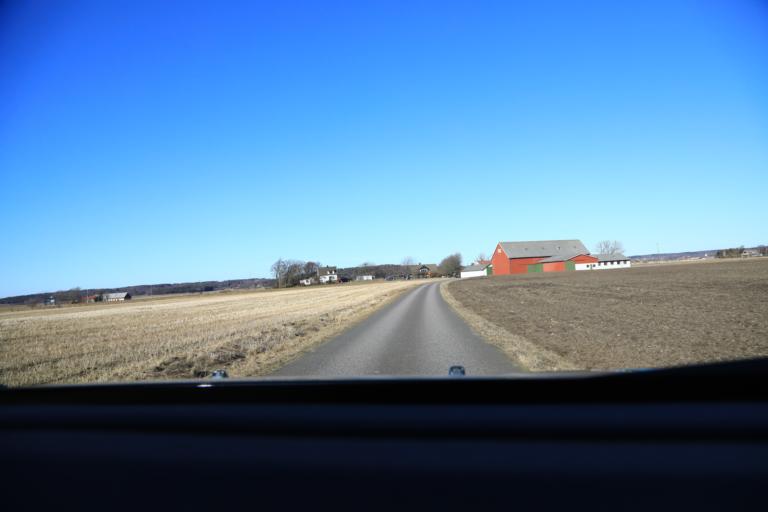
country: SE
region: Halland
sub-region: Kungsbacka Kommun
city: Frillesas
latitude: 57.2329
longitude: 12.1477
